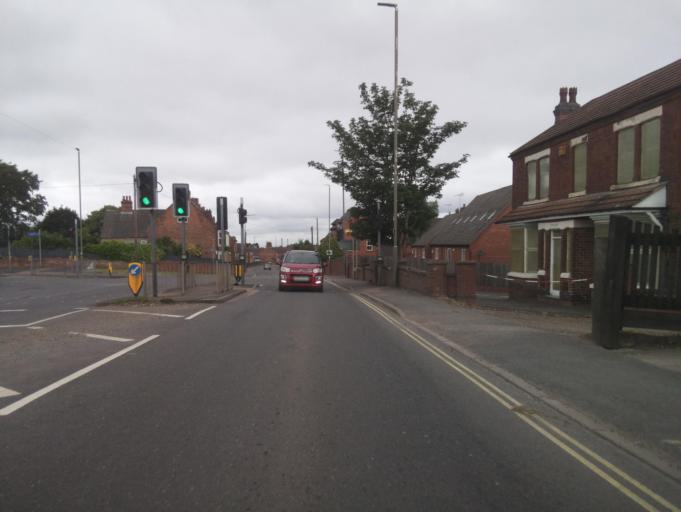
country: GB
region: England
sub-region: Derbyshire
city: Swadlincote
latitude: 52.7656
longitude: -1.5247
